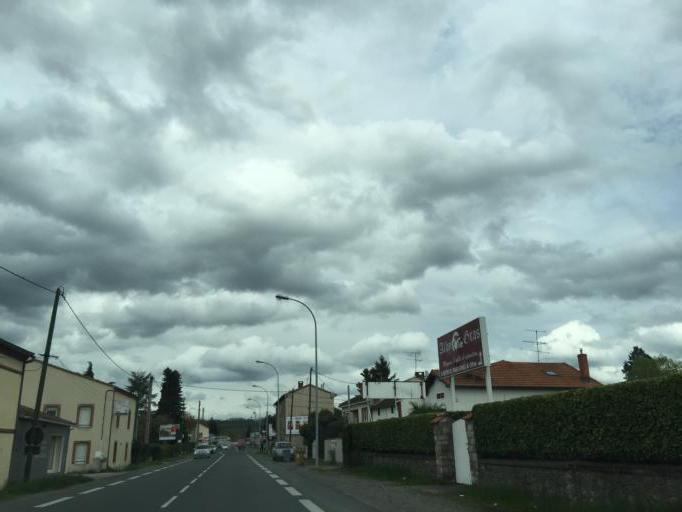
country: FR
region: Midi-Pyrenees
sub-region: Departement du Tarn
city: Albi
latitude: 43.9489
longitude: 2.1529
